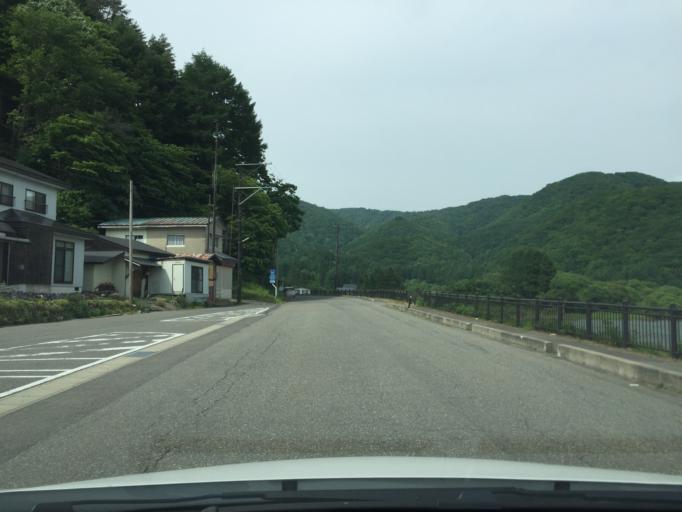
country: JP
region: Fukushima
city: Inawashiro
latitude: 37.7279
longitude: 140.0470
